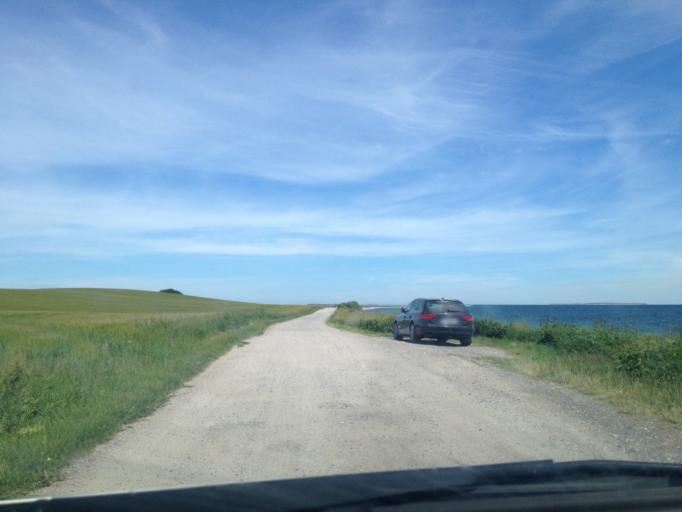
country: DK
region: Central Jutland
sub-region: Samso Kommune
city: Tranebjerg
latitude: 55.8793
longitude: 10.6766
